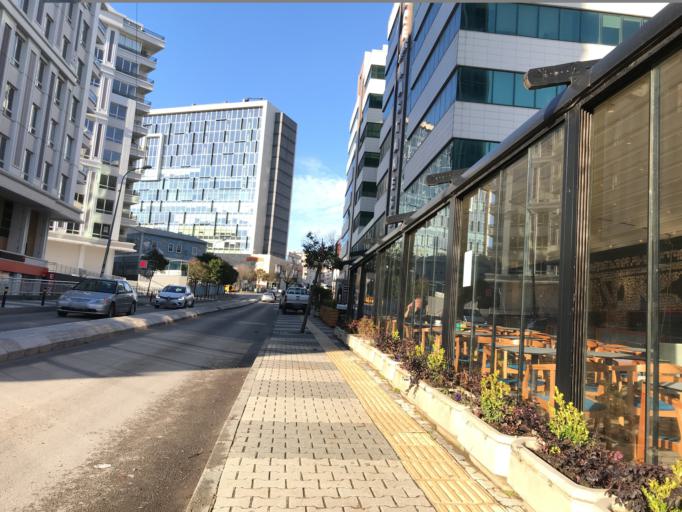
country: TR
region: Istanbul
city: Maltepe
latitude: 40.9364
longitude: 29.1347
